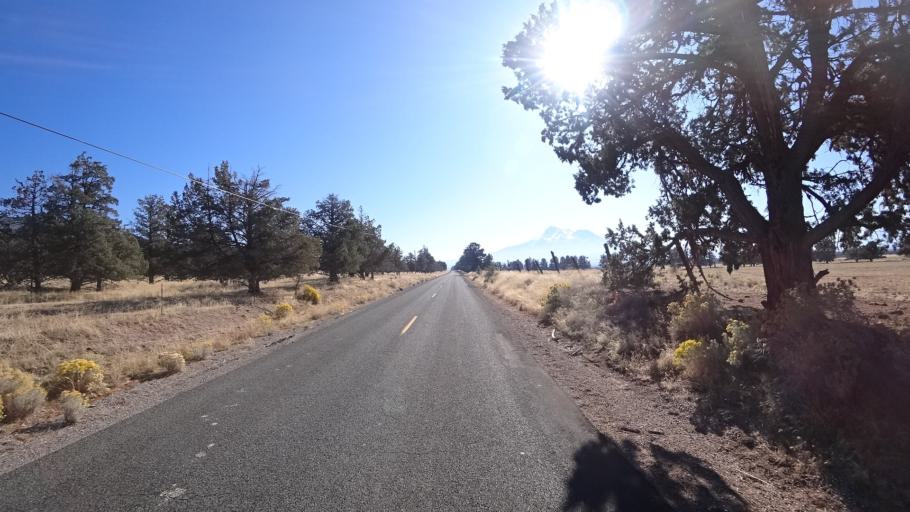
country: US
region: California
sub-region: Siskiyou County
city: Weed
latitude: 41.6268
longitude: -122.3303
